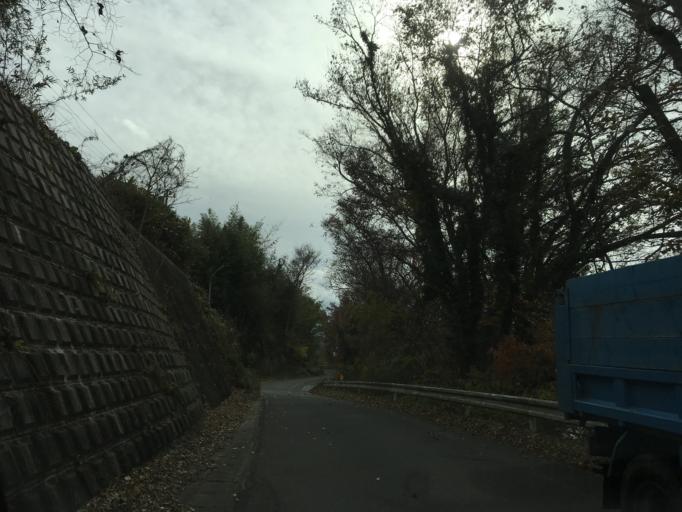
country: JP
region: Iwate
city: Ichinoseki
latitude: 38.7629
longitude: 141.2751
